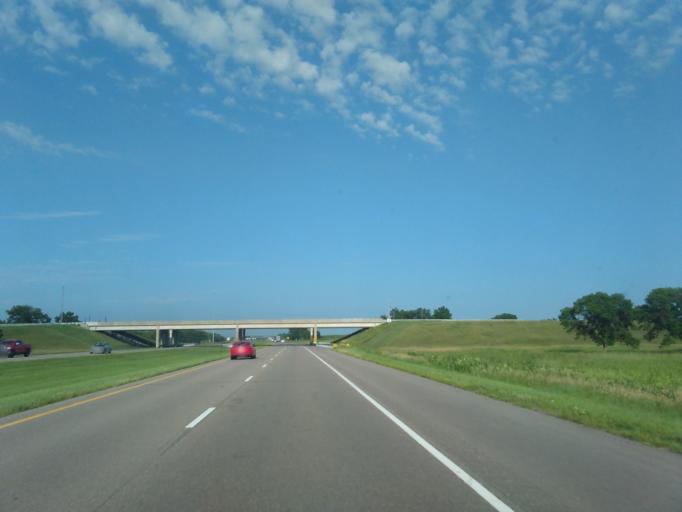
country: US
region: Nebraska
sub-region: York County
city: York
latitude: 40.8211
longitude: -97.5999
